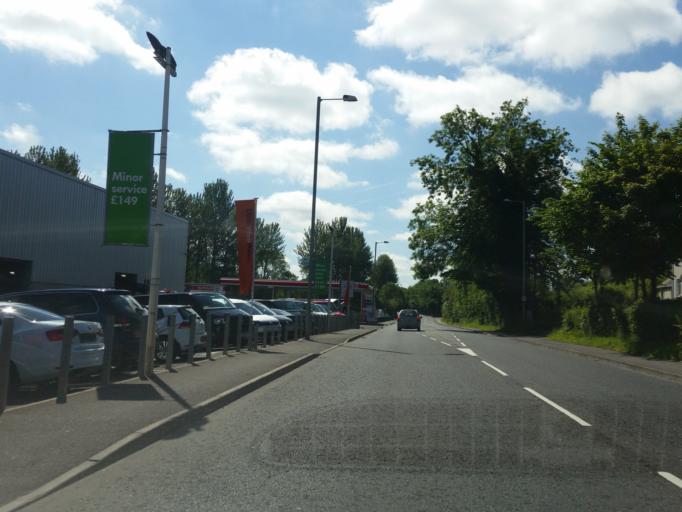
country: GB
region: Northern Ireland
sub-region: Fermanagh District
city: Enniskillen
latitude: 54.3600
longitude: -7.6334
